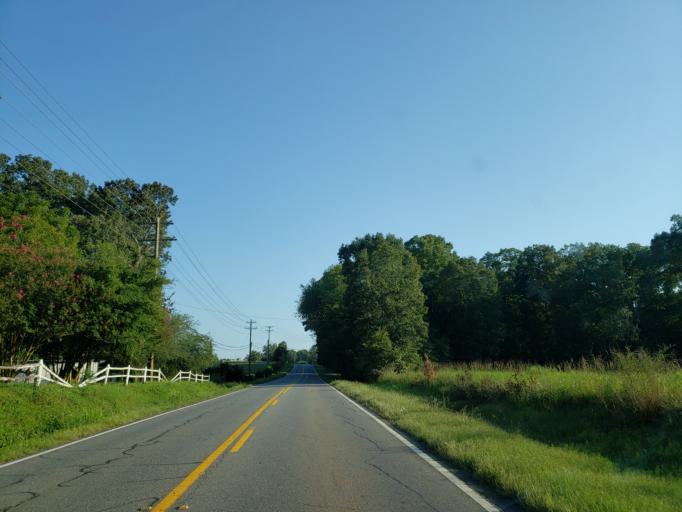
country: US
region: Georgia
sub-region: Murray County
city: Chatsworth
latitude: 34.7756
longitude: -84.8243
